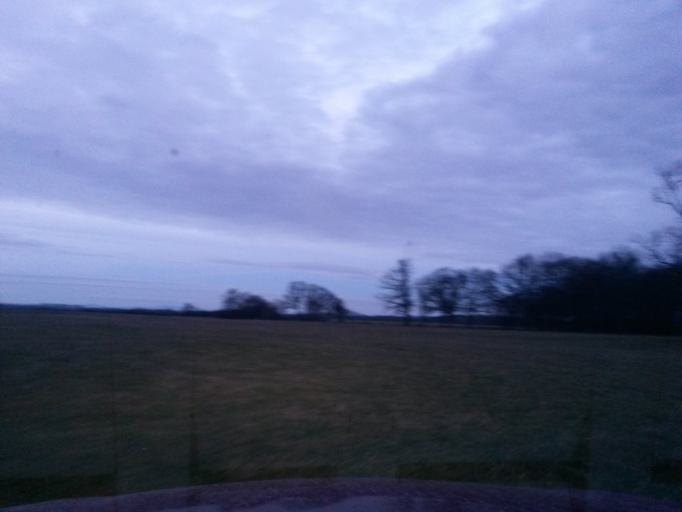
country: HU
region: Borsod-Abauj-Zemplen
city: Karcsa
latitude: 48.4192
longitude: 21.8725
